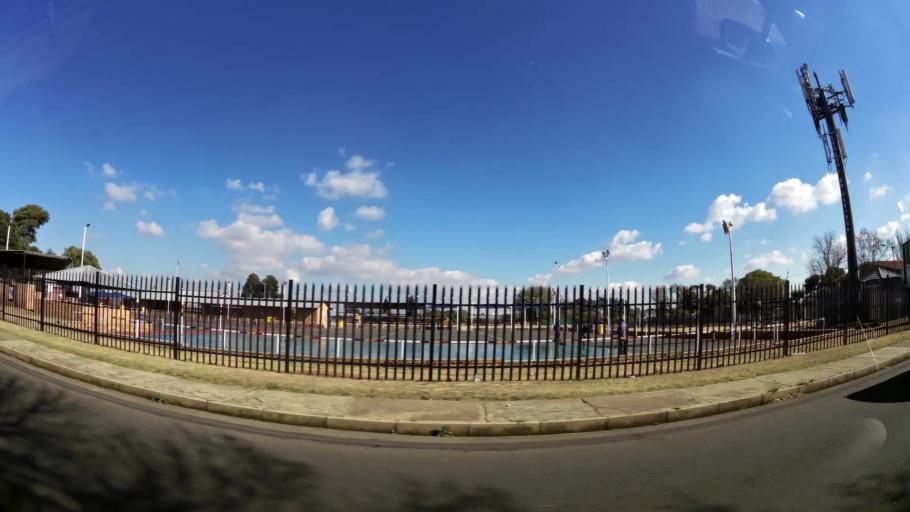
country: ZA
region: Gauteng
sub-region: City of Johannesburg Metropolitan Municipality
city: Roodepoort
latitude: -26.1381
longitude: 27.8365
